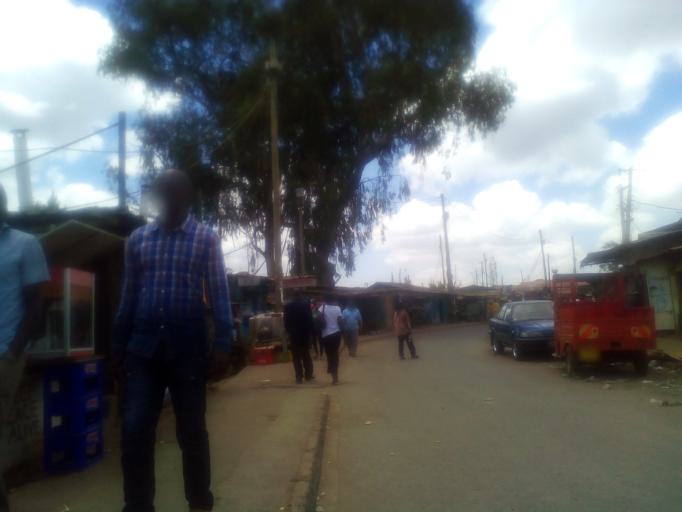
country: KE
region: Nairobi Area
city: Nairobi
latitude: -1.3086
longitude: 36.7855
